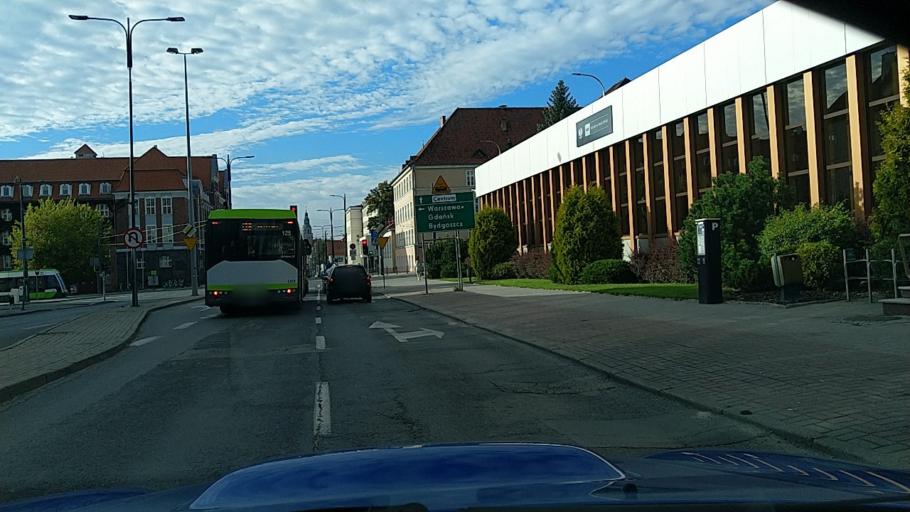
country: PL
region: Warmian-Masurian Voivodeship
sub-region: Powiat olsztynski
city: Olsztyn
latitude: 53.7762
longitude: 20.4889
